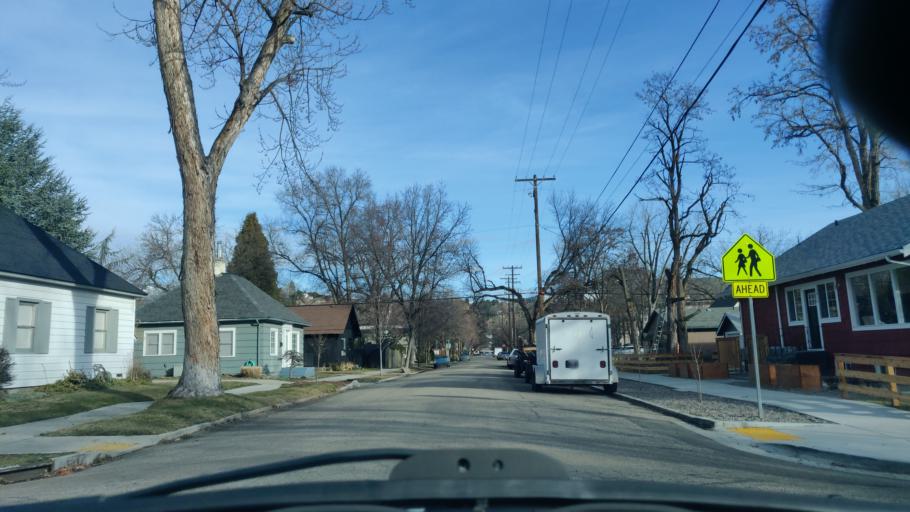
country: US
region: Idaho
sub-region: Ada County
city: Boise
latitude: 43.6284
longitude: -116.2011
